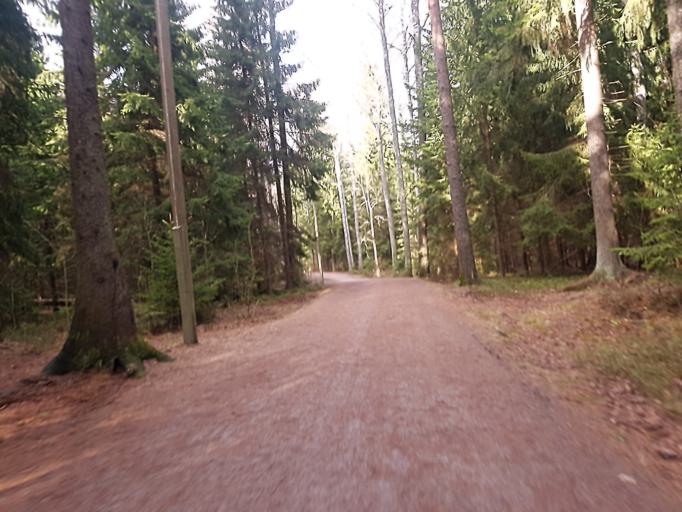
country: FI
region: Uusimaa
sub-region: Helsinki
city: Helsinki
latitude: 60.2581
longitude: 24.9284
